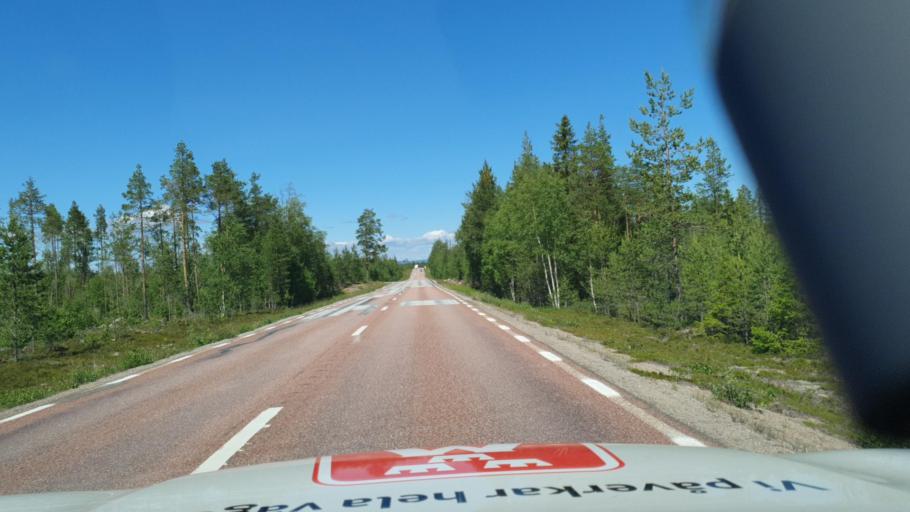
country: SE
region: Jaemtland
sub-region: Harjedalens Kommun
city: Sveg
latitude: 61.8984
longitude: 14.6231
